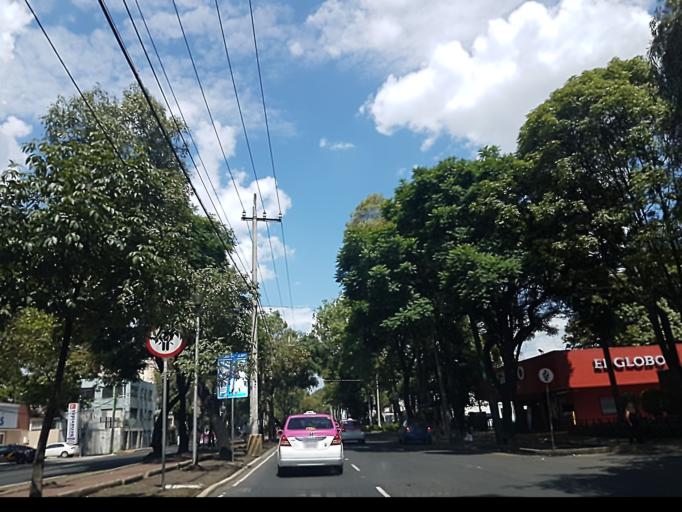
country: MX
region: Mexico City
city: Coyoacan
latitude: 19.3410
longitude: -99.1365
